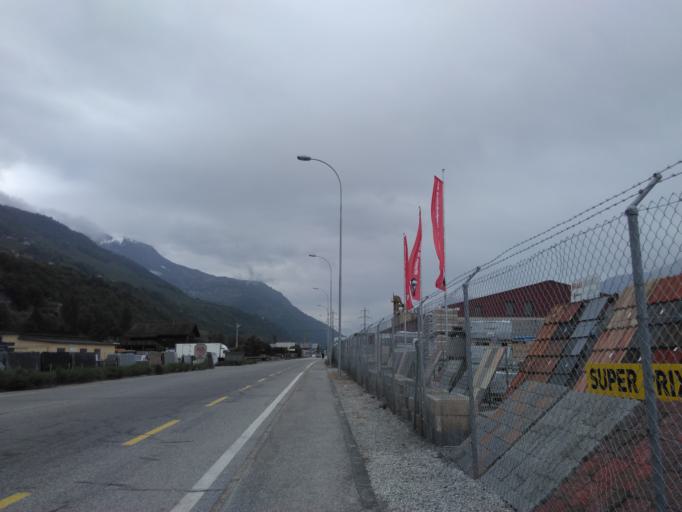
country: CH
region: Valais
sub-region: Sion District
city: Sitten
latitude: 46.2224
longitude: 7.3597
